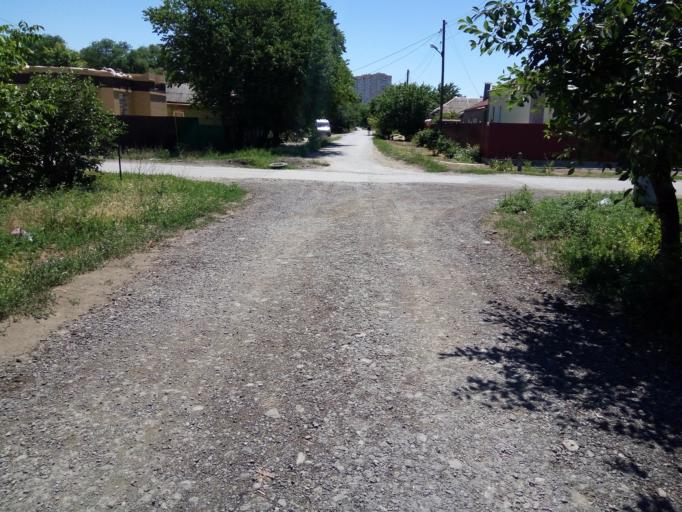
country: RU
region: Rostov
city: Bataysk
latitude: 47.1433
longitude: 39.7709
